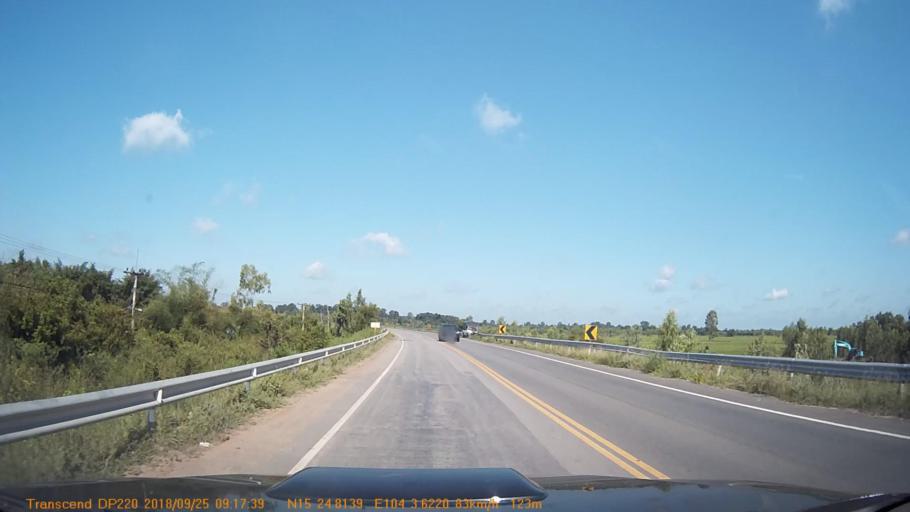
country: TH
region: Sisaket
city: Sila Lat
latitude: 15.4135
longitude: 104.0605
